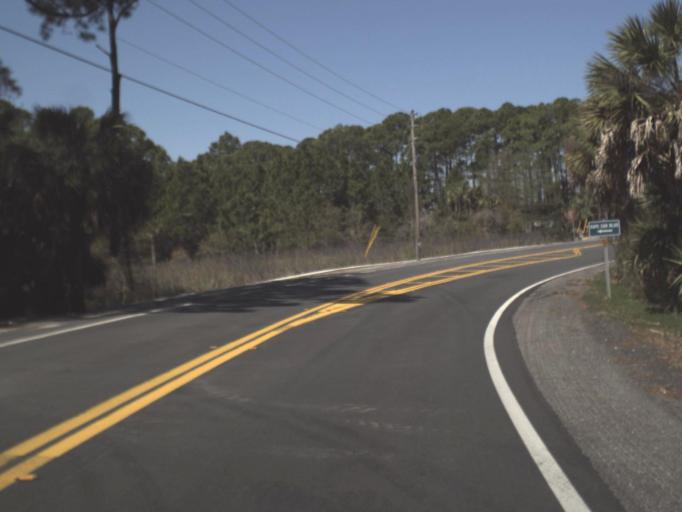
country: US
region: Florida
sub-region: Gulf County
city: Port Saint Joe
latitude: 29.6853
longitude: -85.3083
